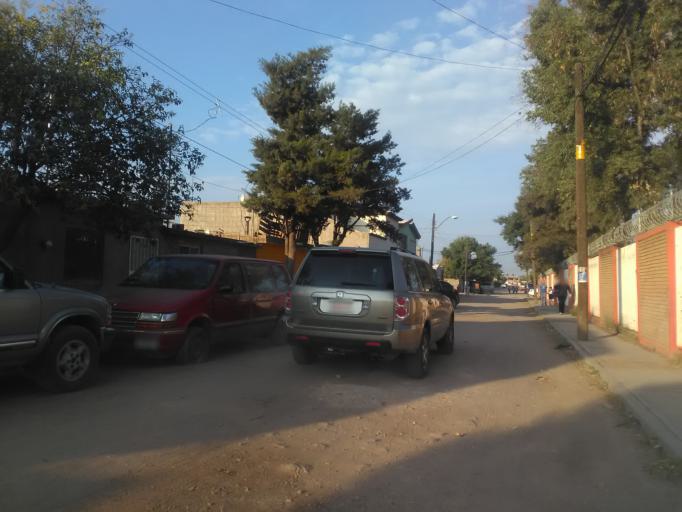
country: MX
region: Durango
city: Victoria de Durango
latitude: 24.0509
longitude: -104.6450
